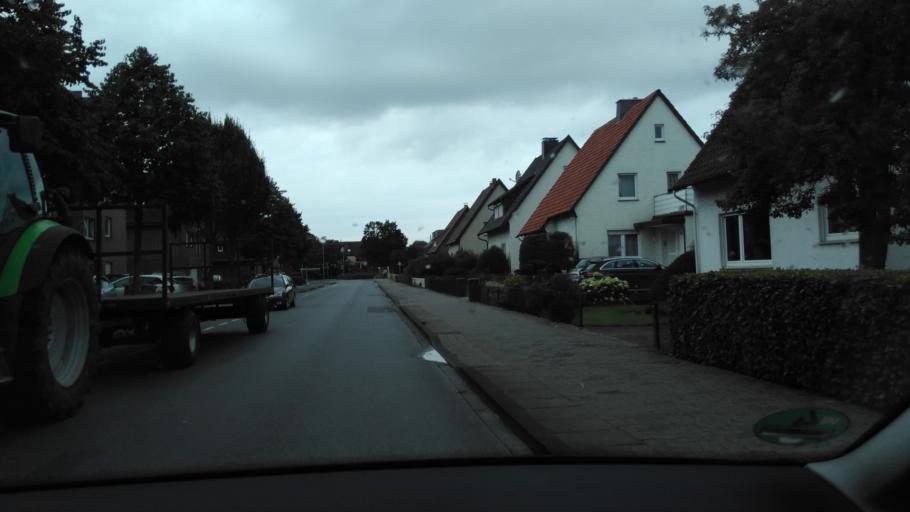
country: DE
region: North Rhine-Westphalia
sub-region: Regierungsbezirk Detmold
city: Guetersloh
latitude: 51.8886
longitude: 8.4293
